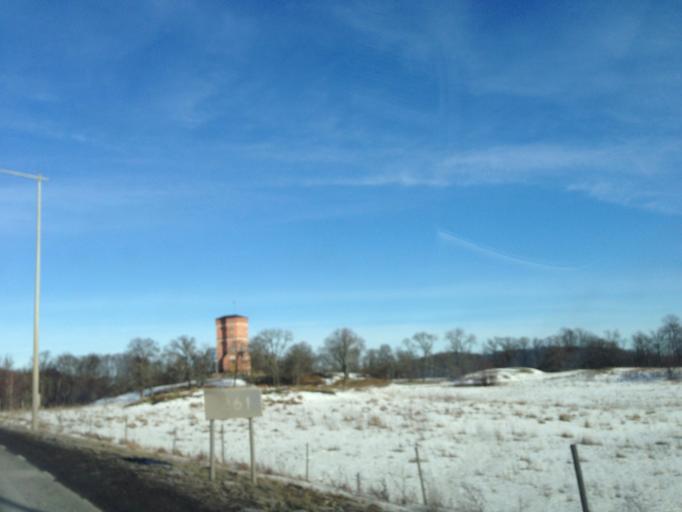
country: SE
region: Stockholm
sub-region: Ekero Kommun
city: Ekeroe
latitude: 59.3210
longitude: 17.8684
